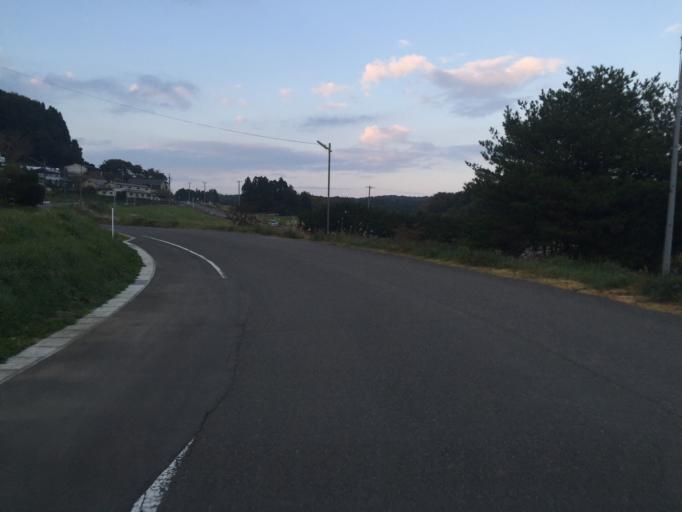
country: JP
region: Fukushima
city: Nihommatsu
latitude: 37.6112
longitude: 140.3571
